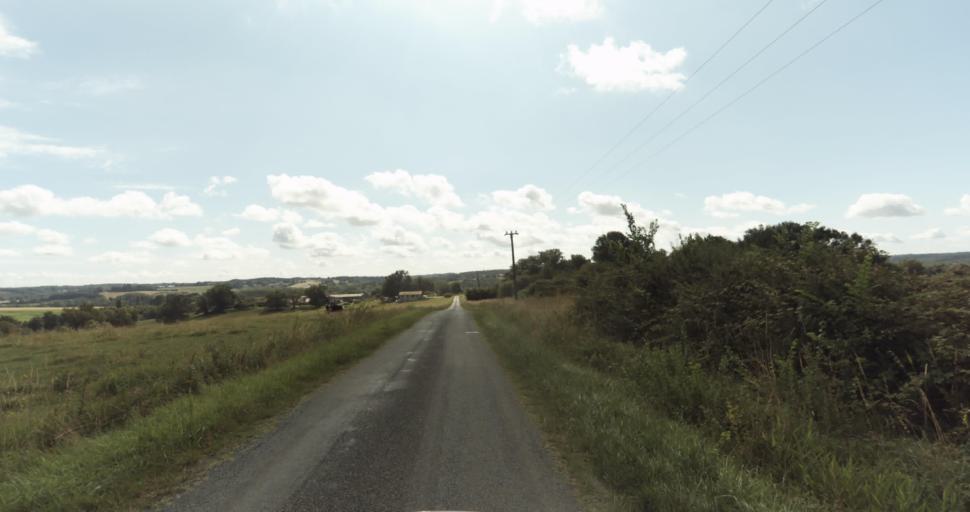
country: FR
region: Aquitaine
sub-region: Departement de la Gironde
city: Bazas
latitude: 44.4500
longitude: -0.1798
